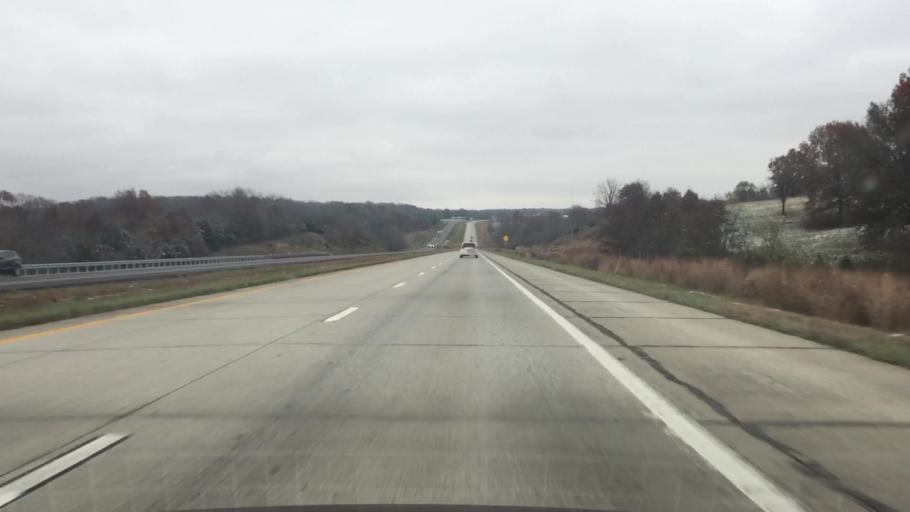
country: US
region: Missouri
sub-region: Saint Clair County
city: Osceola
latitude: 38.0221
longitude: -93.6702
